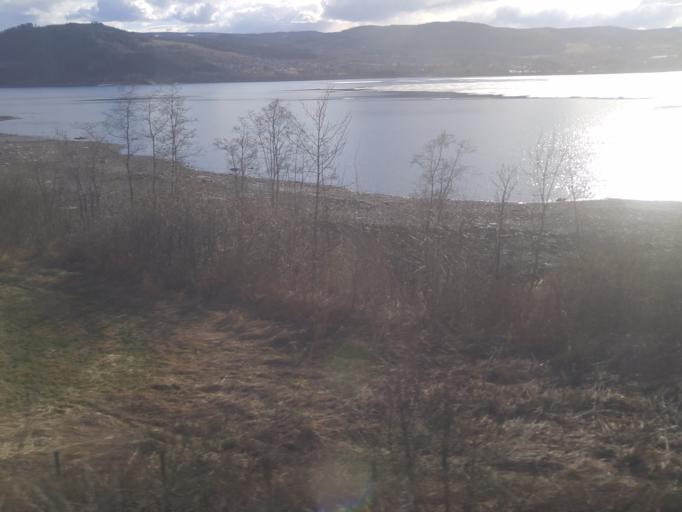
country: NO
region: Hedmark
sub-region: Ringsaker
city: Moelv
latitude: 60.9626
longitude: 10.6650
